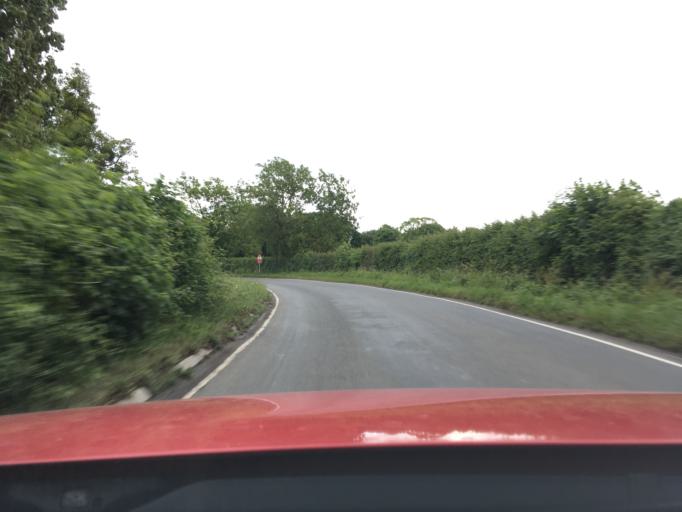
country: GB
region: England
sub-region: Gloucestershire
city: Stonehouse
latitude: 51.7775
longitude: -2.3771
